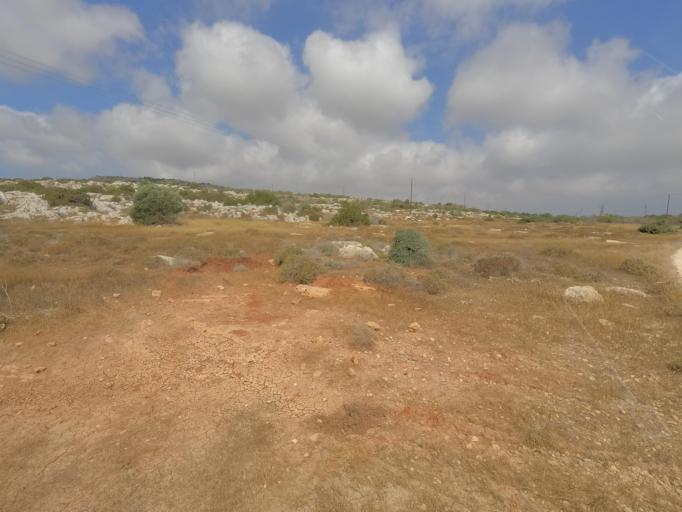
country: CY
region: Ammochostos
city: Protaras
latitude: 35.0066
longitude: 34.0414
